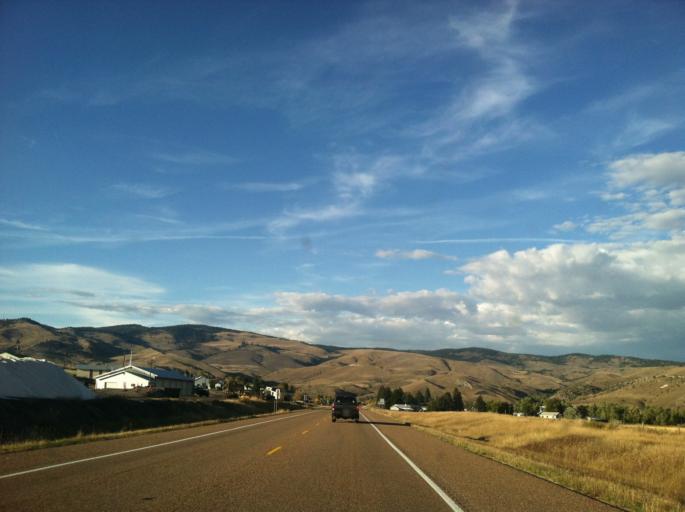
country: US
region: Montana
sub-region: Granite County
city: Philipsburg
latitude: 46.6563
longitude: -113.1594
